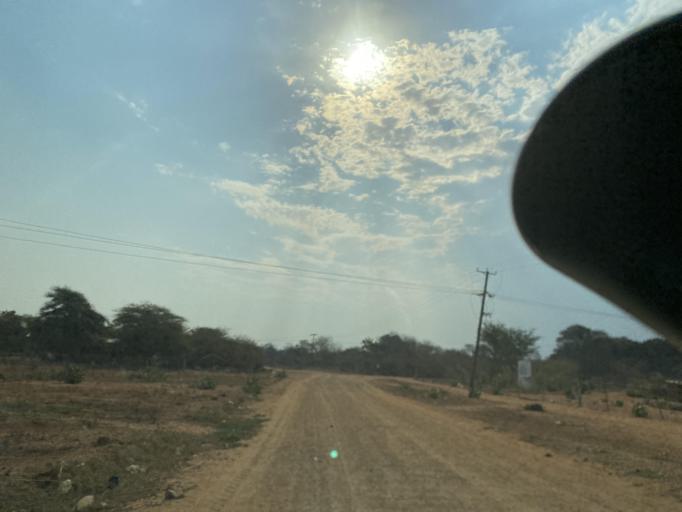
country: ZW
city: Chirundu
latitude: -15.9348
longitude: 28.9375
